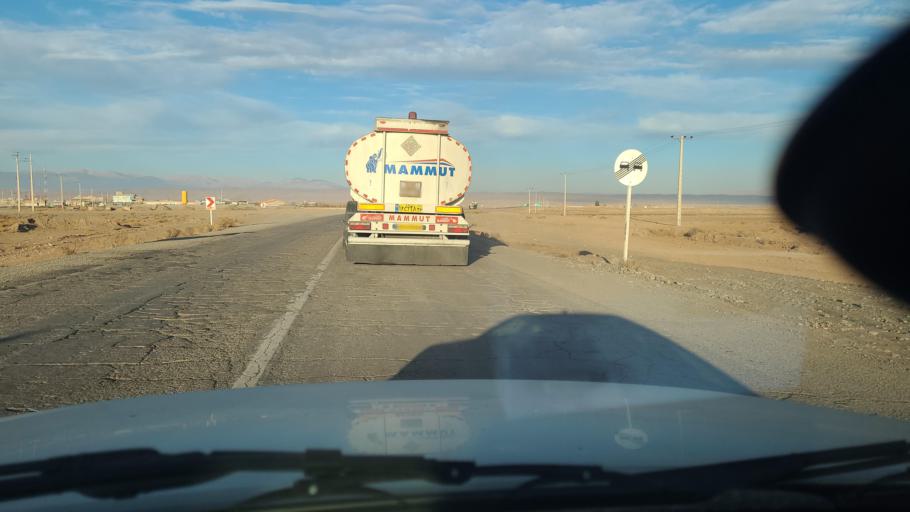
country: IR
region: Razavi Khorasan
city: Neqab
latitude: 36.6124
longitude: 57.5949
